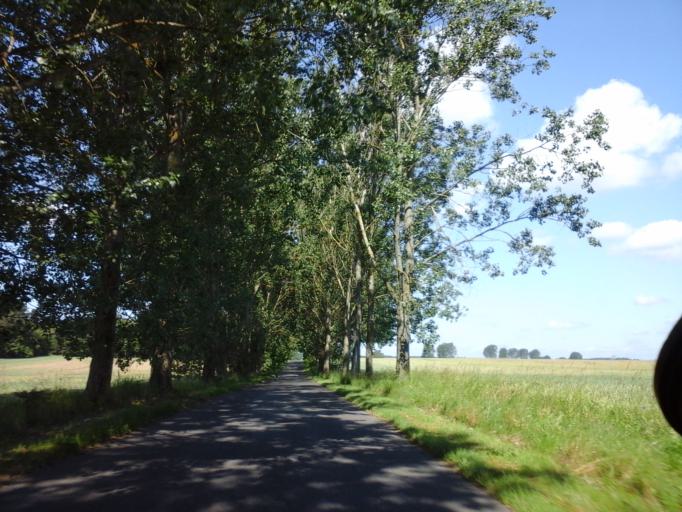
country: PL
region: West Pomeranian Voivodeship
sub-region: Powiat choszczenski
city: Recz
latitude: 53.1969
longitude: 15.5676
